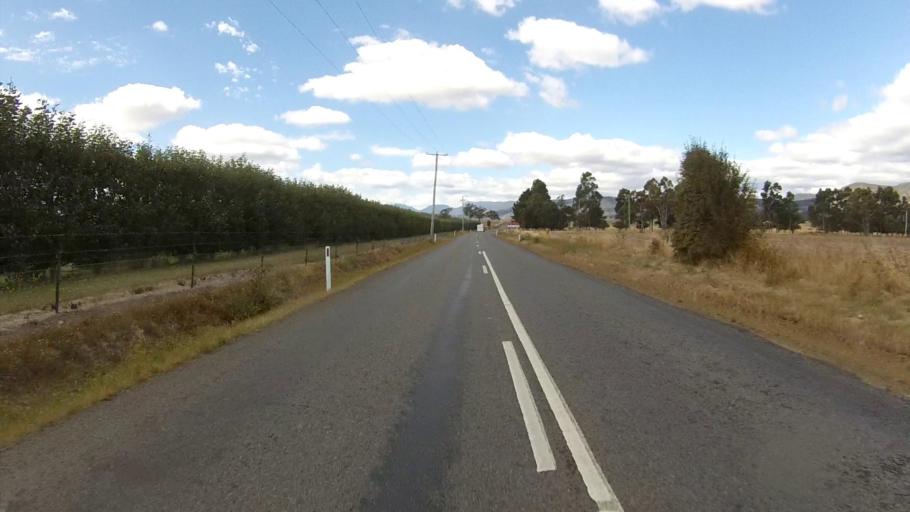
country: AU
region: Tasmania
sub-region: Derwent Valley
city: New Norfolk
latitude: -42.7484
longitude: 146.9731
